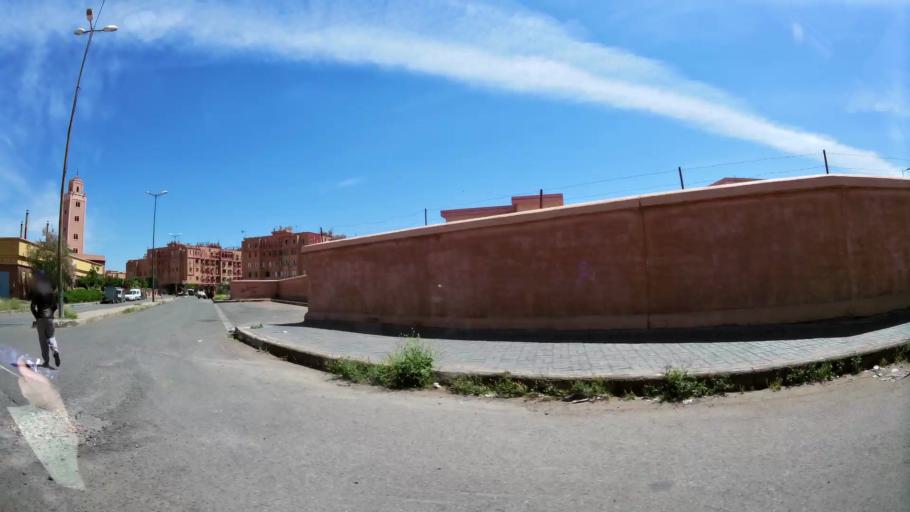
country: MA
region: Marrakech-Tensift-Al Haouz
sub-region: Marrakech
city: Marrakesh
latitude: 31.6485
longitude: -8.0665
